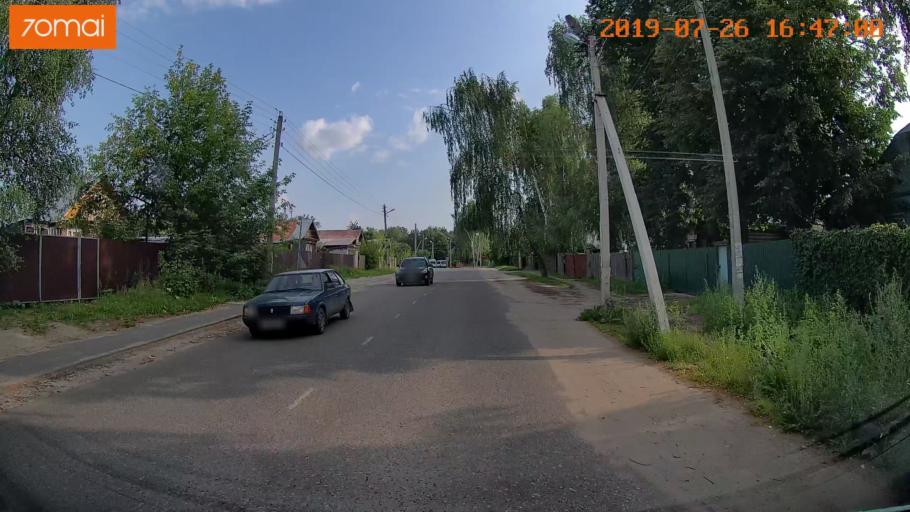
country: RU
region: Ivanovo
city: Bogorodskoye
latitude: 57.0447
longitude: 41.0115
